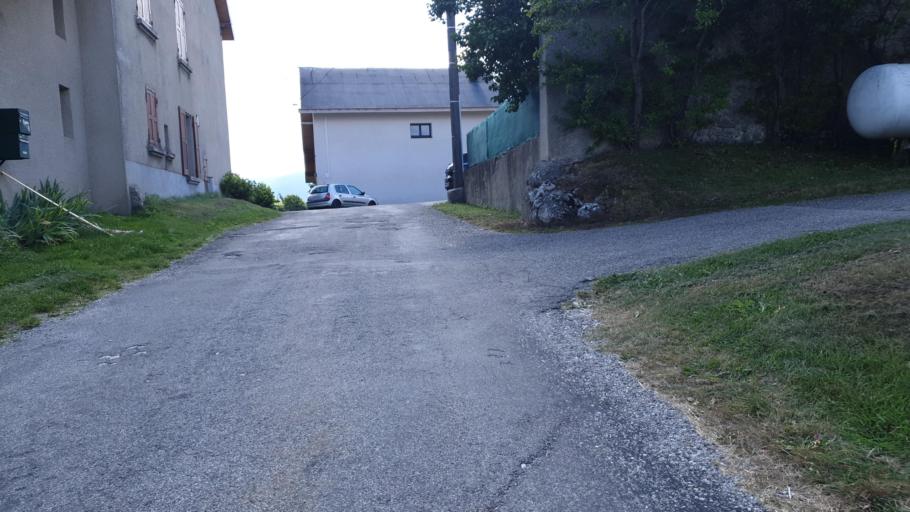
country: FR
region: Rhone-Alpes
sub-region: Departement de l'Isere
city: Autrans
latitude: 45.1775
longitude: 5.5515
